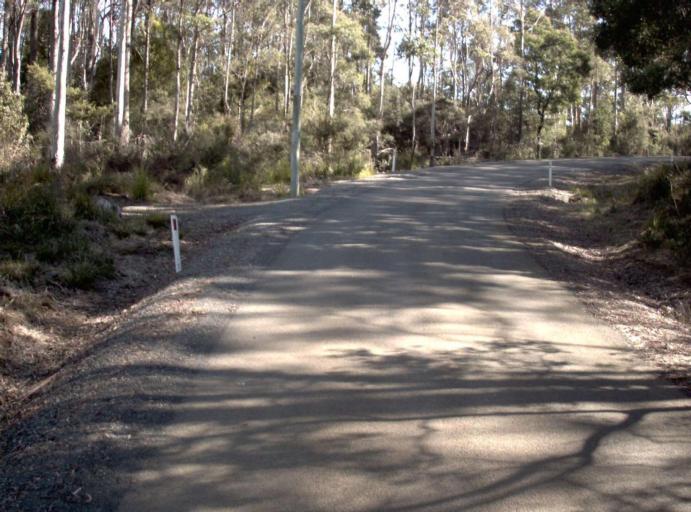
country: AU
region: Tasmania
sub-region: Launceston
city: Mayfield
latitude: -41.3192
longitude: 147.2110
